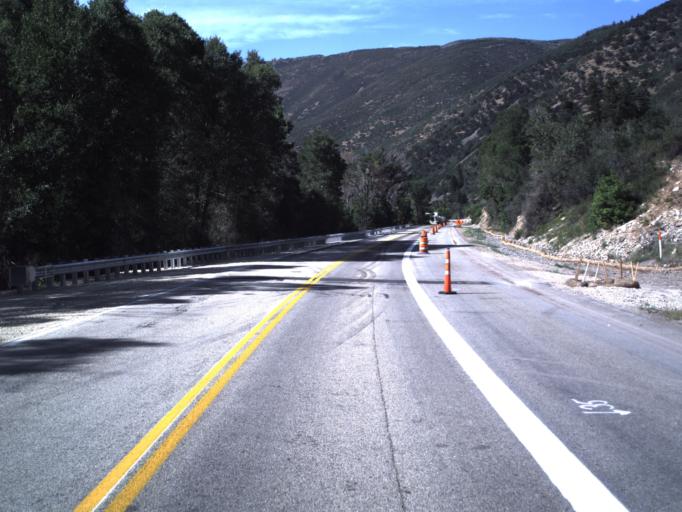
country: US
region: Utah
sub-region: Wasatch County
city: Heber
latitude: 40.3879
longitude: -111.3032
